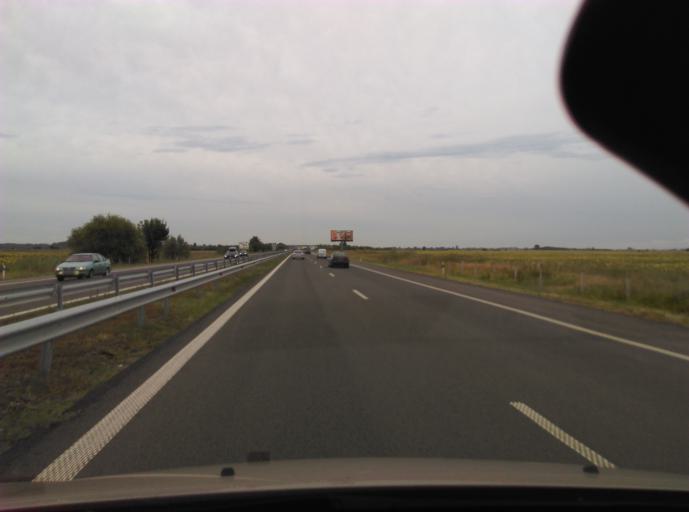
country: BG
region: Plovdiv
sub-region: Obshtina Plovdiv
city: Plovdiv
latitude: 42.2133
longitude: 24.8233
